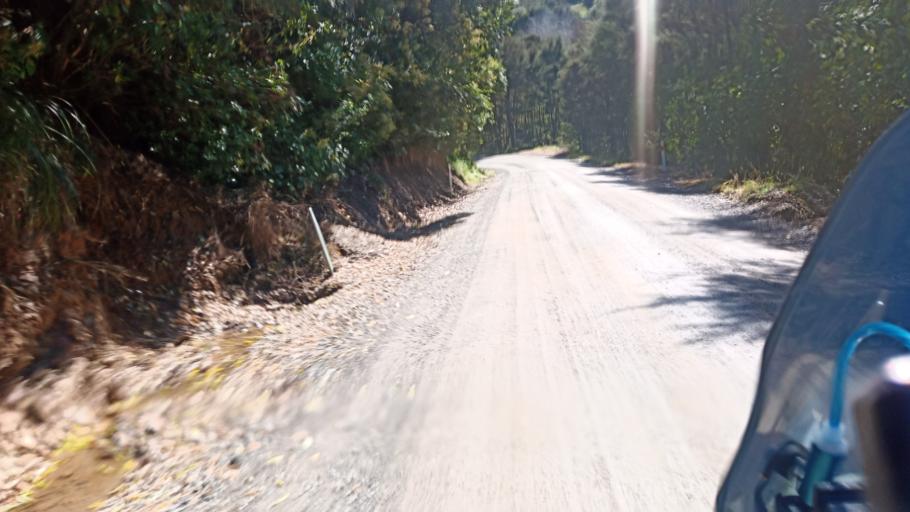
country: NZ
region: Gisborne
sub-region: Gisborne District
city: Gisborne
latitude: -37.9925
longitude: 178.3024
